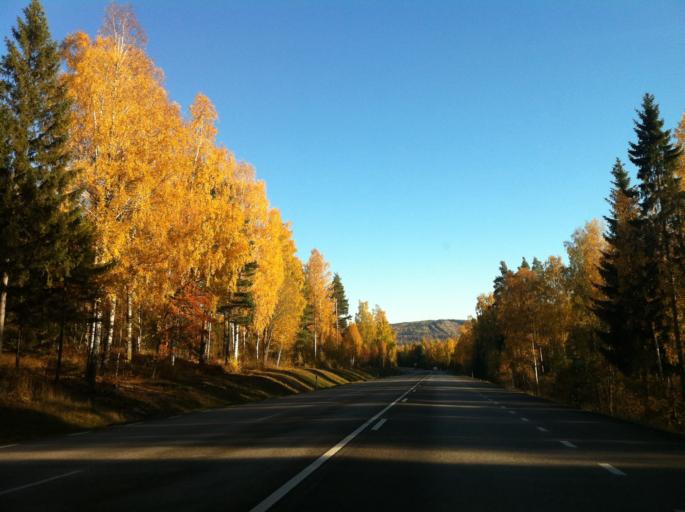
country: SE
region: Dalarna
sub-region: Rattviks Kommun
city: Raettvik
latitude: 60.9002
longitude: 15.0812
